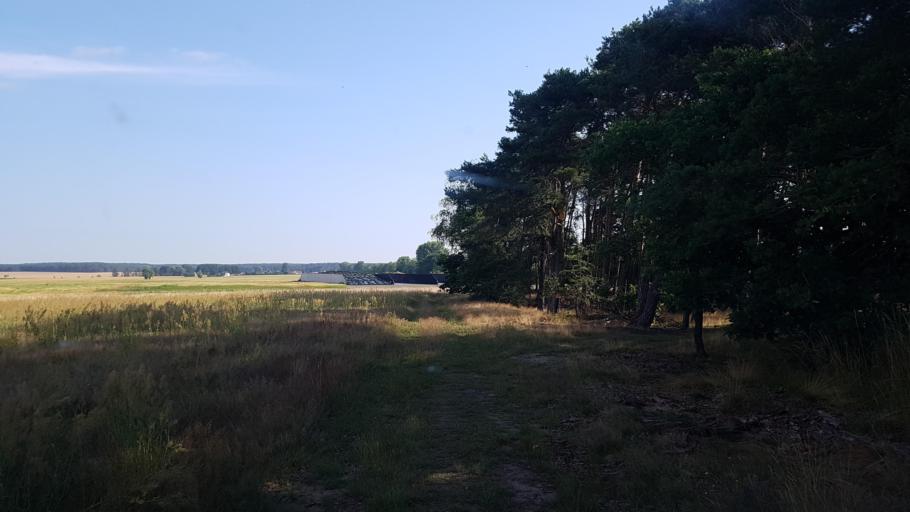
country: DE
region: Brandenburg
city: Finsterwalde
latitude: 51.6929
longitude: 13.7205
